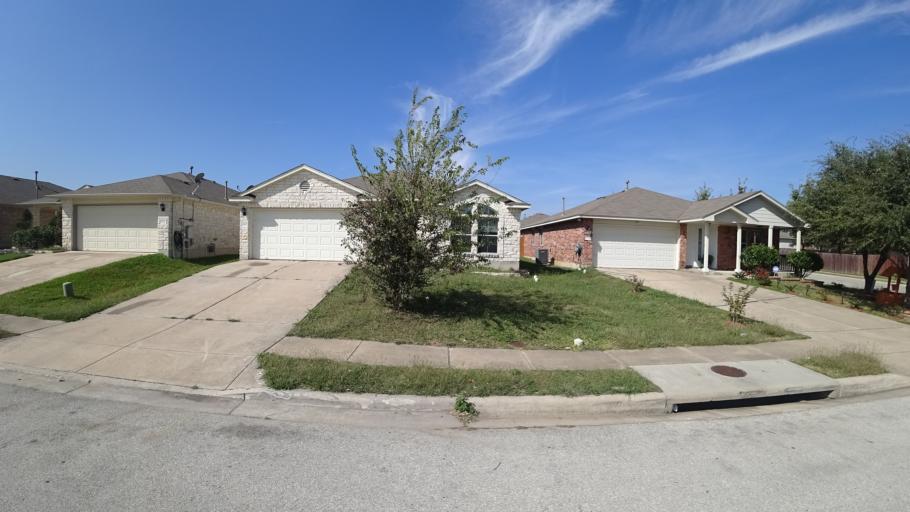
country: US
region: Texas
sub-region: Travis County
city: Pflugerville
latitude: 30.4252
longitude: -97.6350
